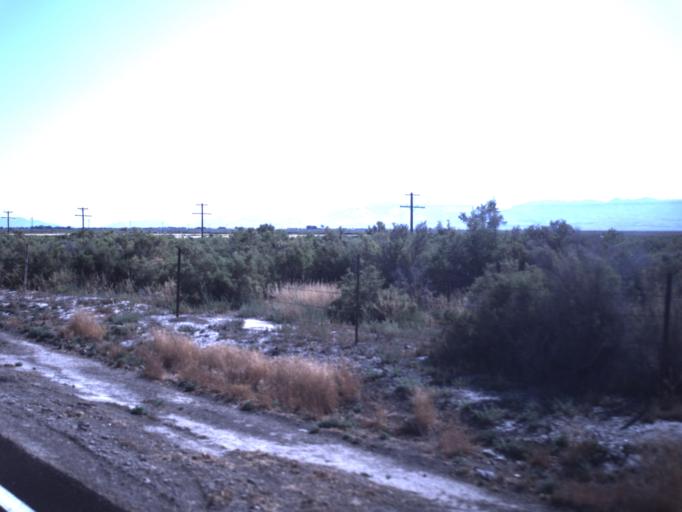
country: US
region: Utah
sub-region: Millard County
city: Delta
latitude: 39.2534
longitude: -112.6547
